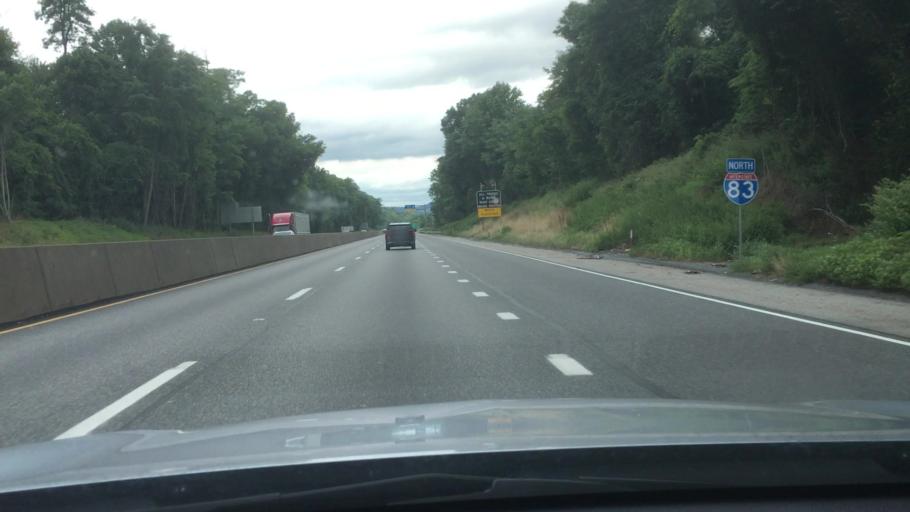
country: US
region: Pennsylvania
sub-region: York County
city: Valley Green
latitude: 40.1346
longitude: -76.8005
